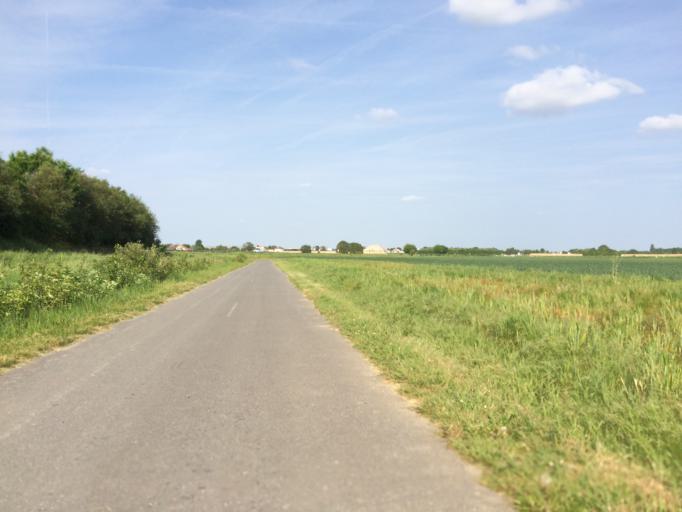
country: FR
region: Ile-de-France
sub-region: Departement de l'Essonne
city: Chilly-Mazarin
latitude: 48.7134
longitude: 2.3184
